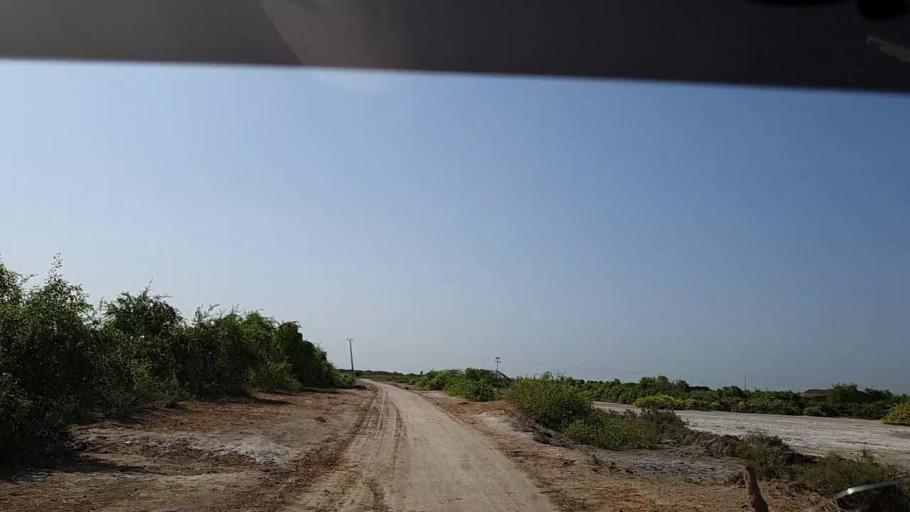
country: PK
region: Sindh
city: Badin
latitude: 24.6201
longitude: 68.7789
